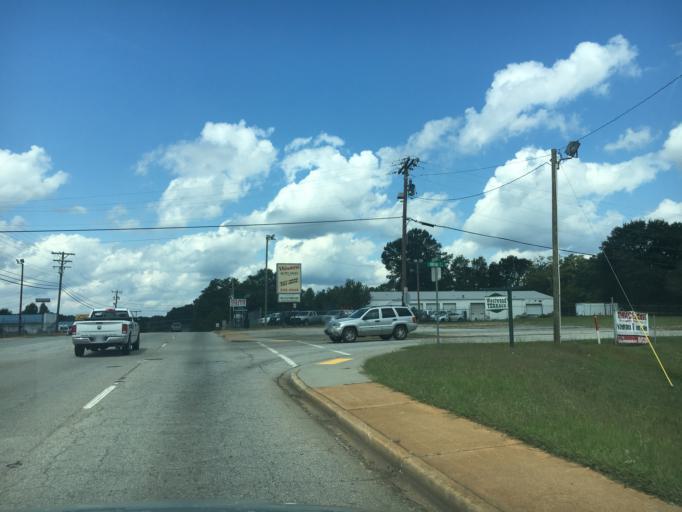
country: US
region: South Carolina
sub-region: Greenville County
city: Berea
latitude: 34.8770
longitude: -82.4442
